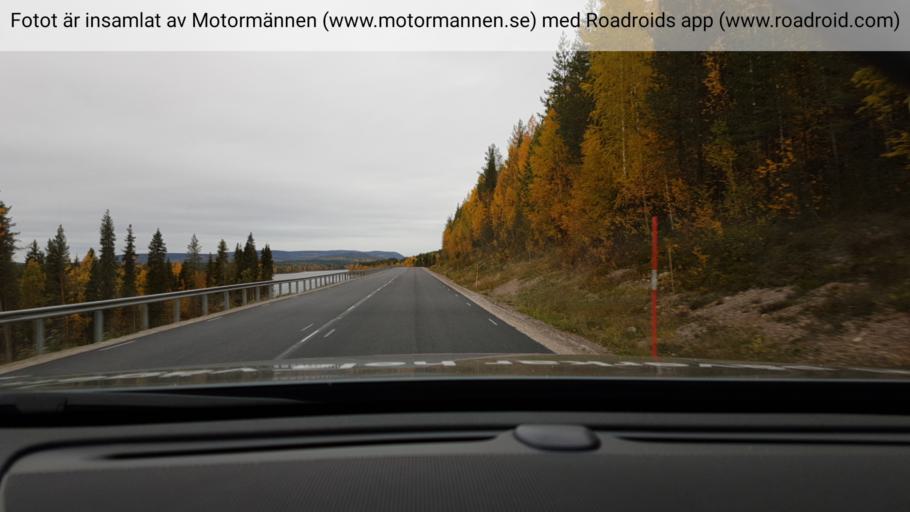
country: SE
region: Norrbotten
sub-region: Overkalix Kommun
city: OEverkalix
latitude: 66.4762
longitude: 22.7888
